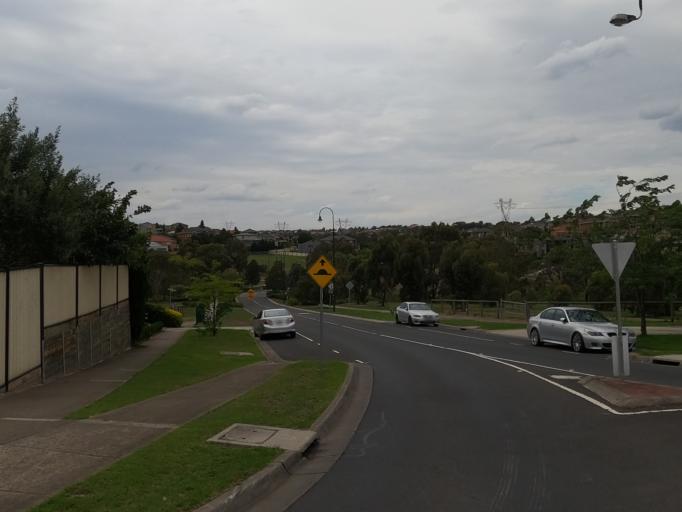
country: AU
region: Victoria
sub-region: Hume
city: Meadow Heights
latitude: -37.6461
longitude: 144.9042
